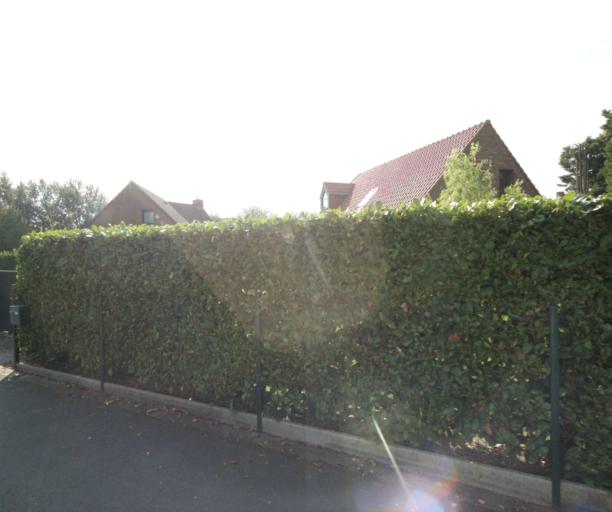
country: FR
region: Nord-Pas-de-Calais
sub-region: Departement du Nord
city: Wattignies
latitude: 50.5747
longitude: 3.0250
